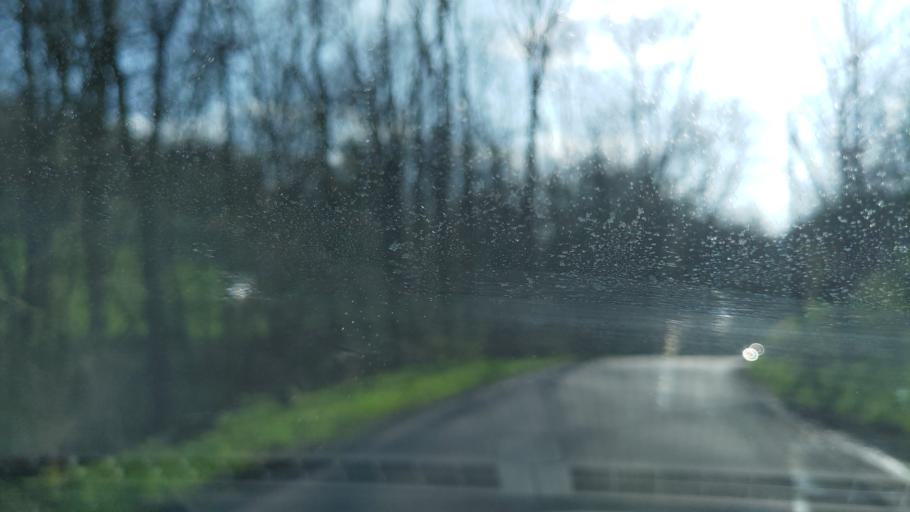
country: CZ
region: Ustecky
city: Povrly
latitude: 50.7081
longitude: 14.2135
